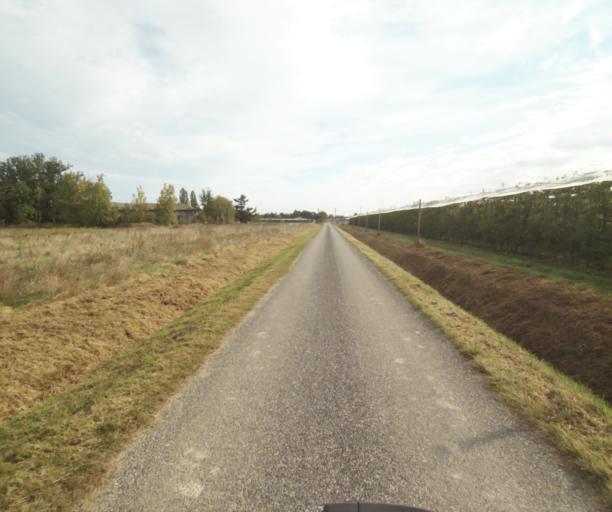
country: FR
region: Midi-Pyrenees
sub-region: Departement du Tarn-et-Garonne
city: Montech
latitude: 43.9404
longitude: 1.2272
